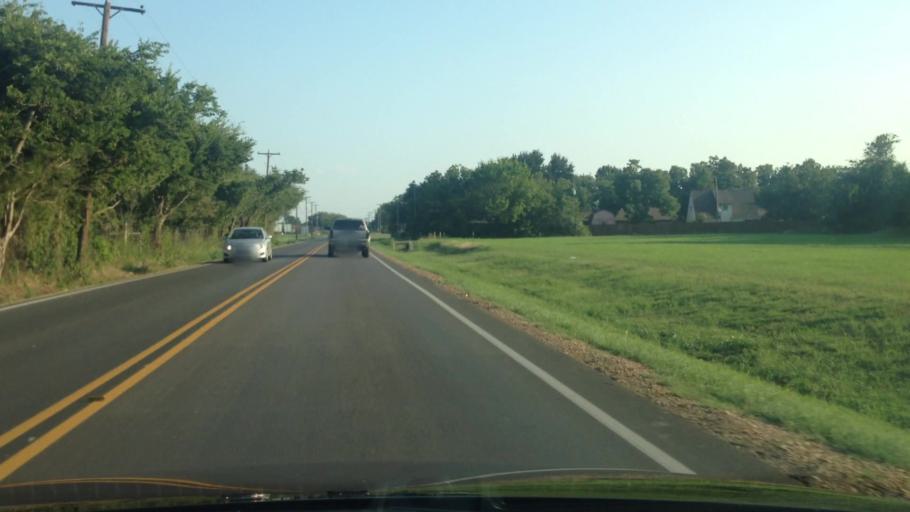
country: US
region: Texas
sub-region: Tarrant County
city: Everman
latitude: 32.6268
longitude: -97.2700
